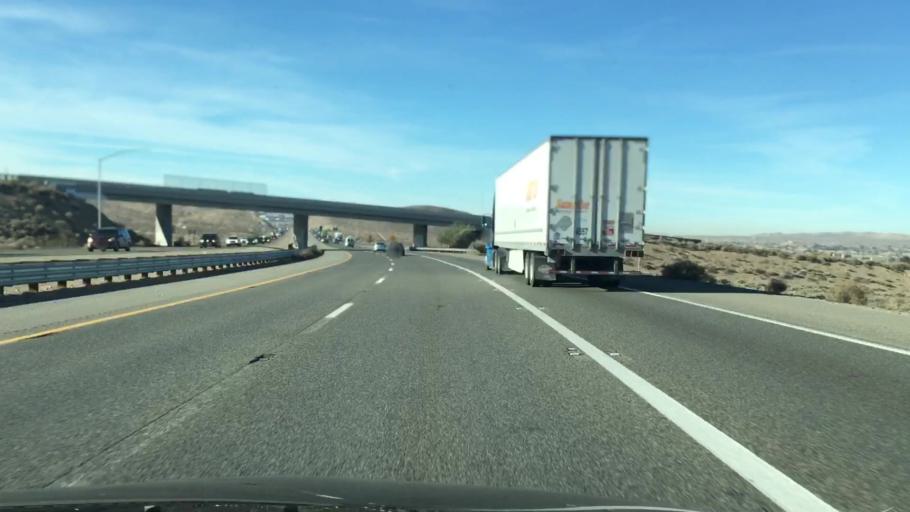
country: US
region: California
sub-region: San Bernardino County
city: Barstow
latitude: 34.9084
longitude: -116.9716
